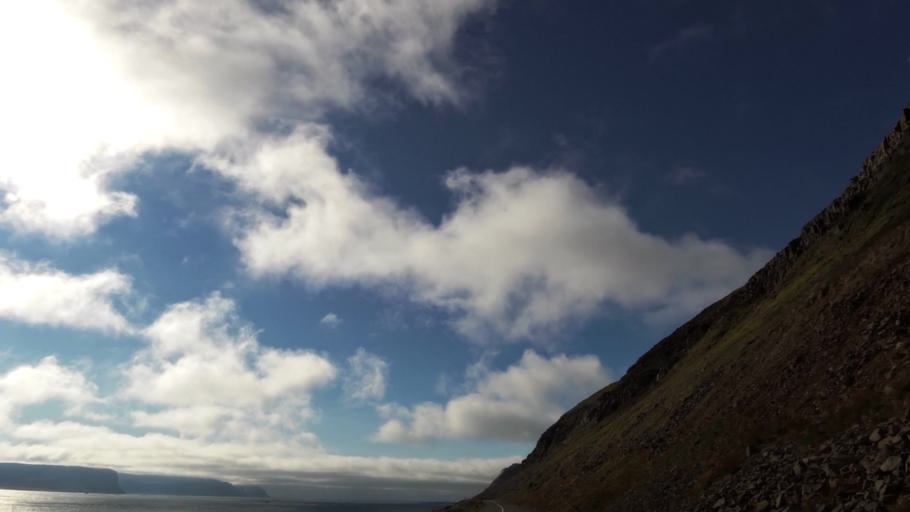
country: IS
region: West
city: Olafsvik
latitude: 65.5666
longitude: -23.9234
